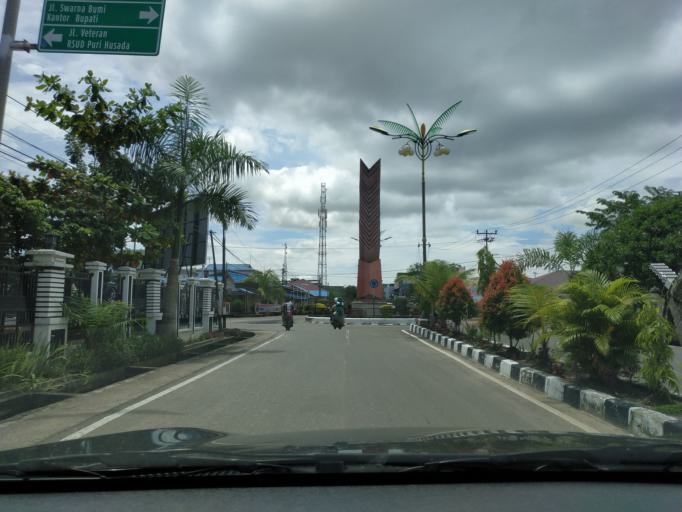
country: ID
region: Riau
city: Tembilahan
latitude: -0.3213
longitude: 103.1620
